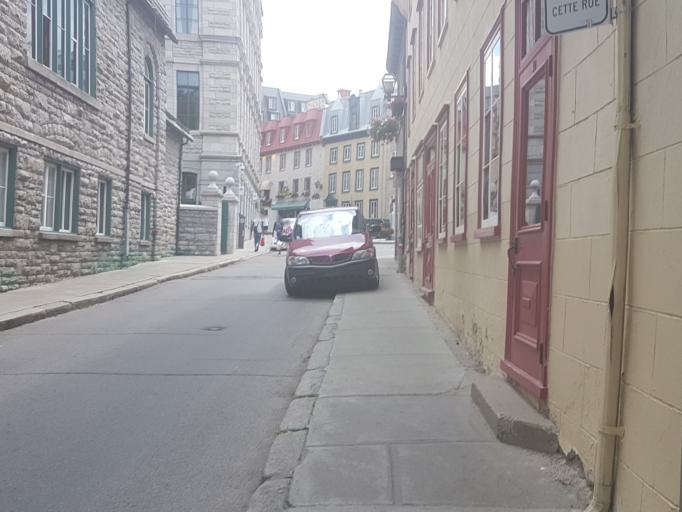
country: CA
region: Quebec
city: Quebec
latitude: 46.8126
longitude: -71.2075
